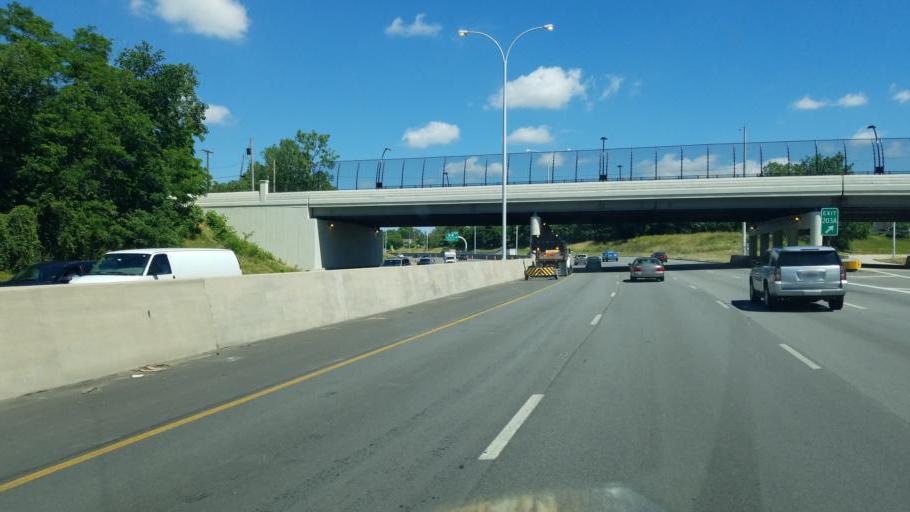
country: US
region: Ohio
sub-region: Lucas County
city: Toledo
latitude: 41.6630
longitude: -83.5639
